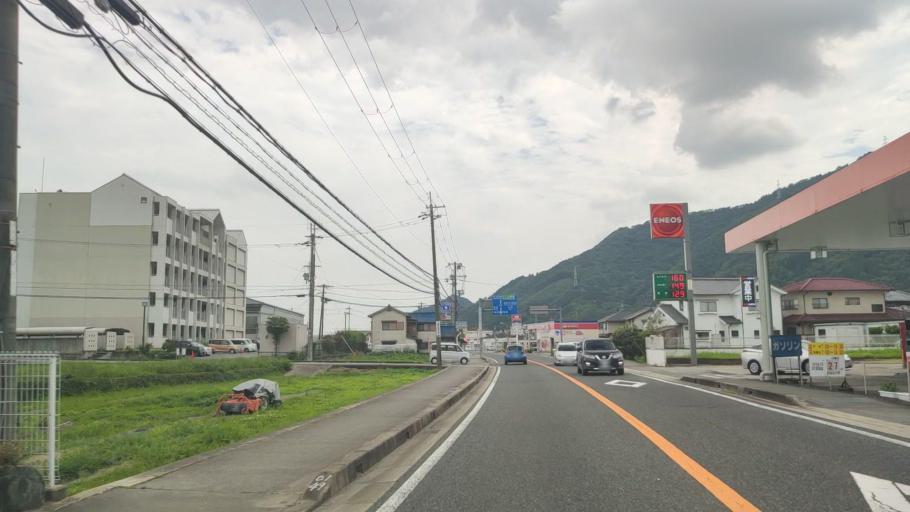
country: JP
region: Hyogo
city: Tatsunocho-tominaga
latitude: 34.8961
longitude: 134.5463
